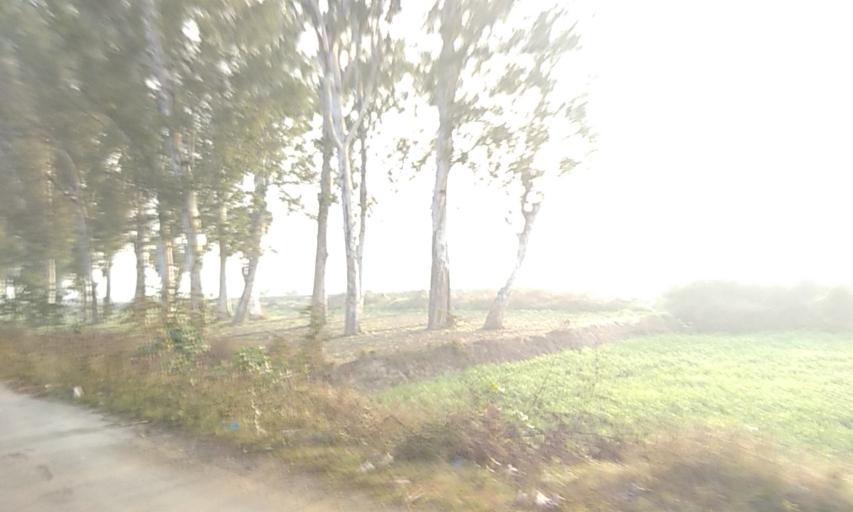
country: IN
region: Punjab
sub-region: Gurdaspur
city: Dhariwal
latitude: 31.9373
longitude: 75.3086
